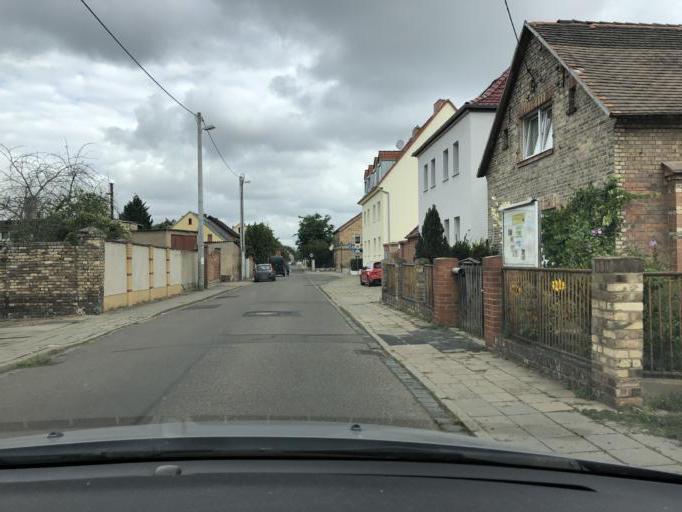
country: DE
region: Saxony-Anhalt
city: Dollnitz
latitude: 51.4089
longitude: 12.0296
